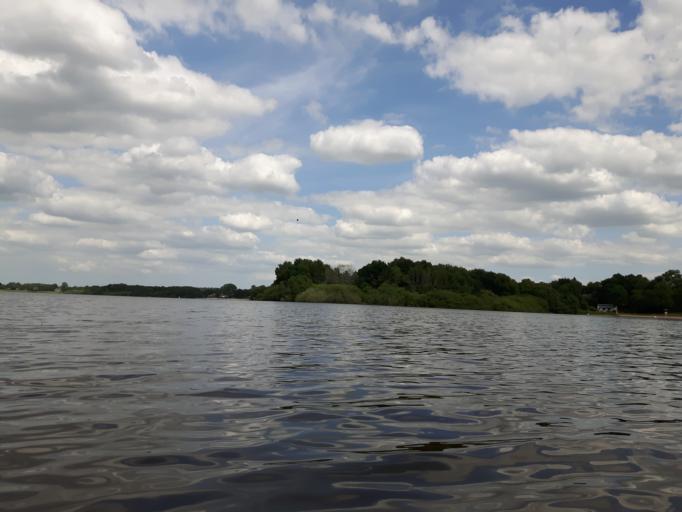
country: DE
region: Schleswig-Holstein
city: Muhbrook
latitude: 54.1332
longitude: 9.9935
